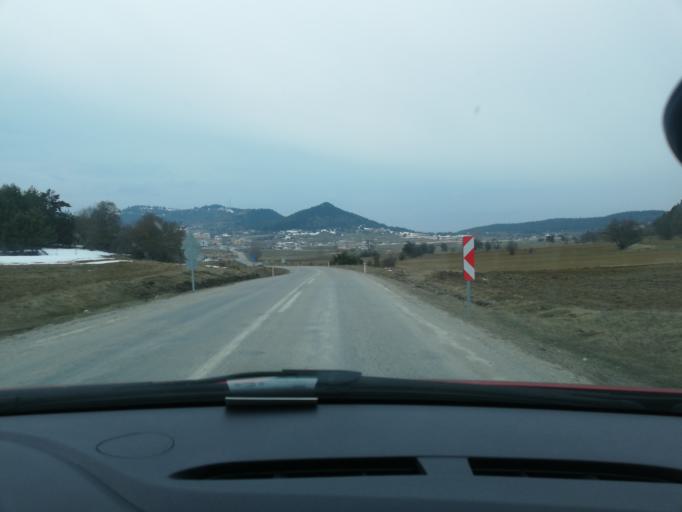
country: TR
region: Kastamonu
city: Agli
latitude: 41.6899
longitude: 33.5680
